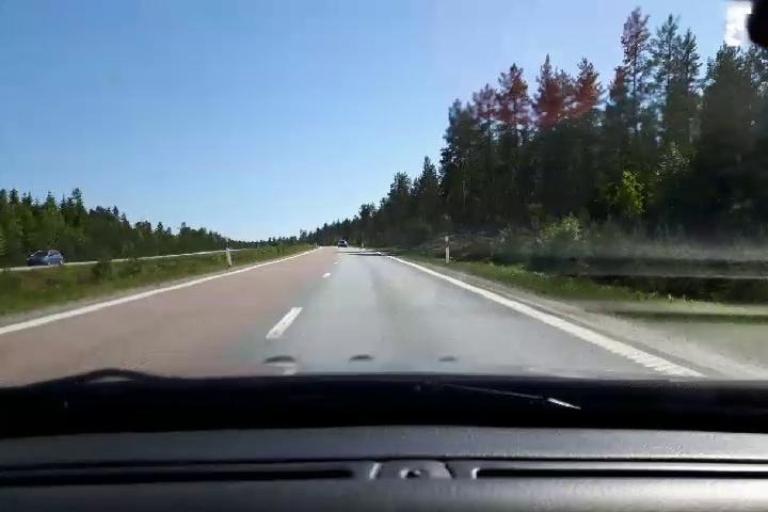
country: SE
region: Gaevleborg
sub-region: Soderhamns Kommun
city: Soderhamn
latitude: 61.4627
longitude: 16.9881
